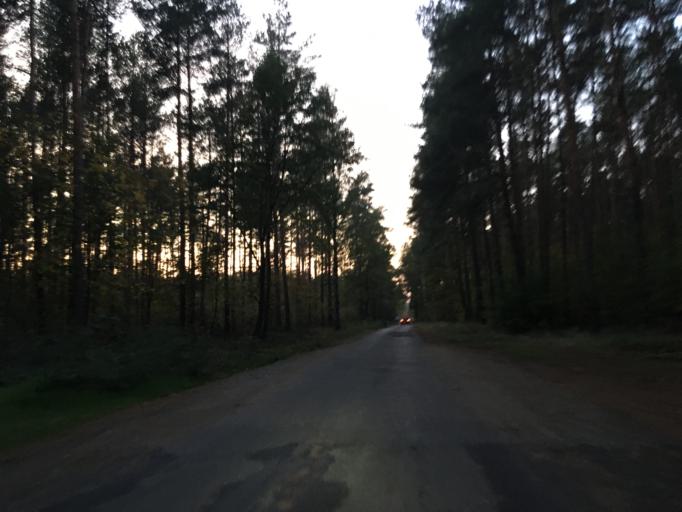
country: DE
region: Brandenburg
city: Birkenwerder
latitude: 52.6835
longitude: 13.3250
